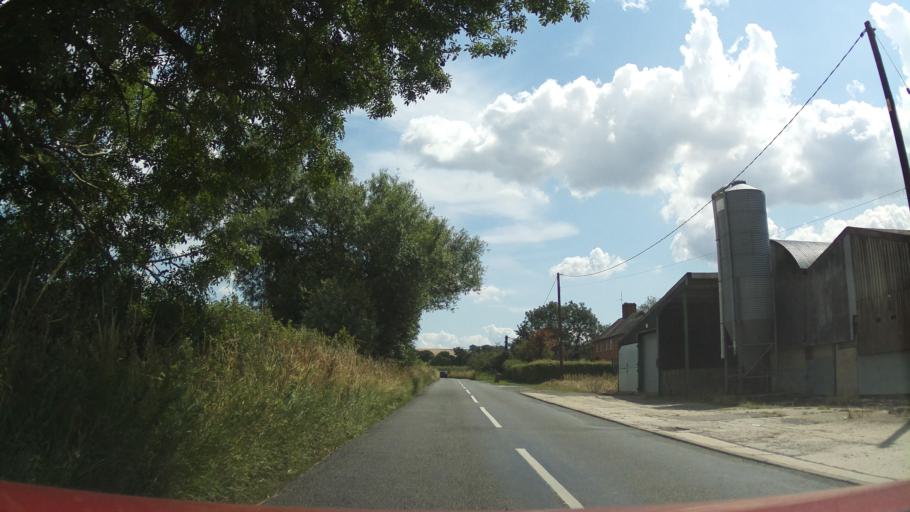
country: GB
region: England
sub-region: Borough of Swindon
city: Bishopstone
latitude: 51.5735
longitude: -1.6353
